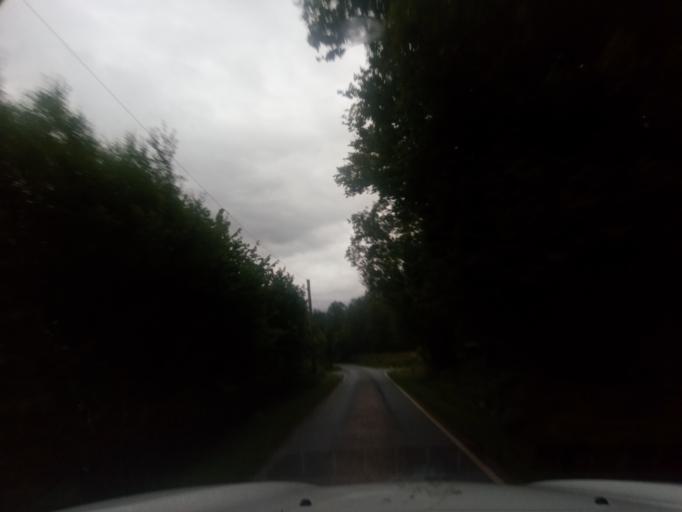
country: GB
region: Scotland
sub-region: Highland
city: Fort William
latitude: 56.8460
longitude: -5.2829
